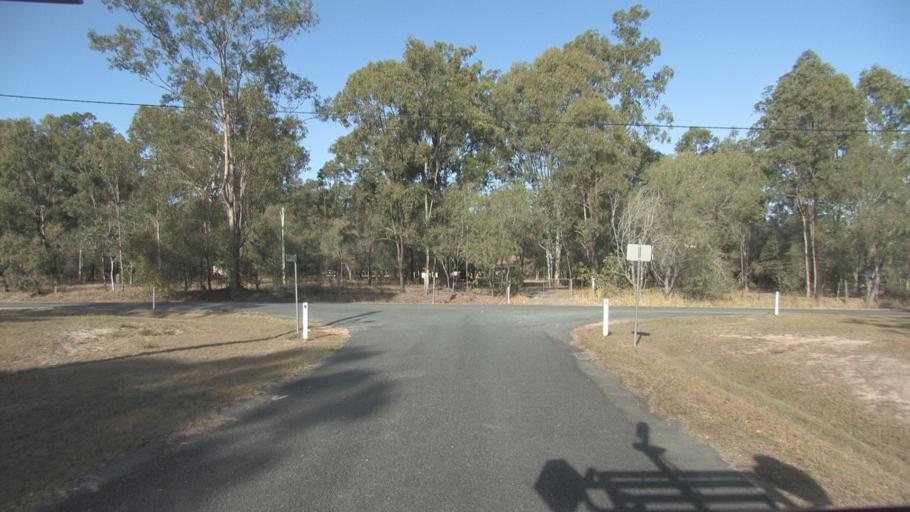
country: AU
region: Queensland
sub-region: Logan
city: North Maclean
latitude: -27.8071
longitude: 152.9760
